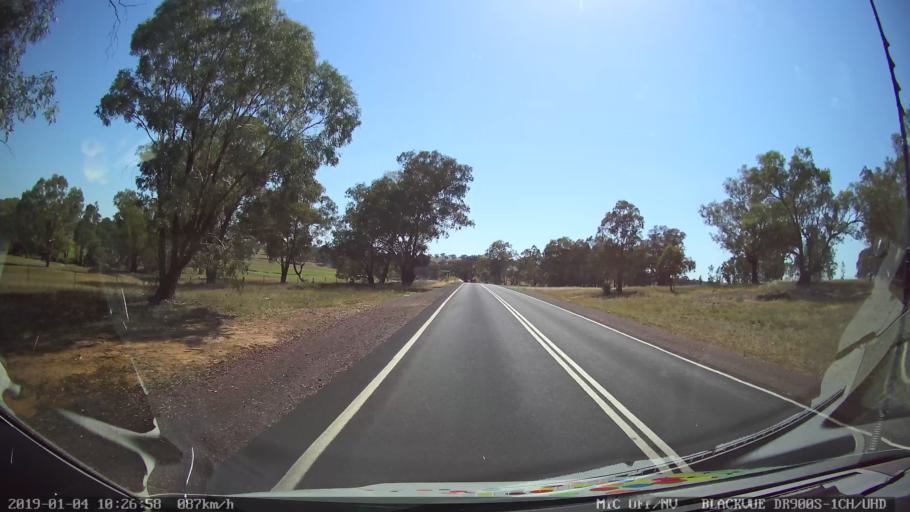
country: AU
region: New South Wales
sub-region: Cabonne
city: Canowindra
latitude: -33.3742
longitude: 148.5932
